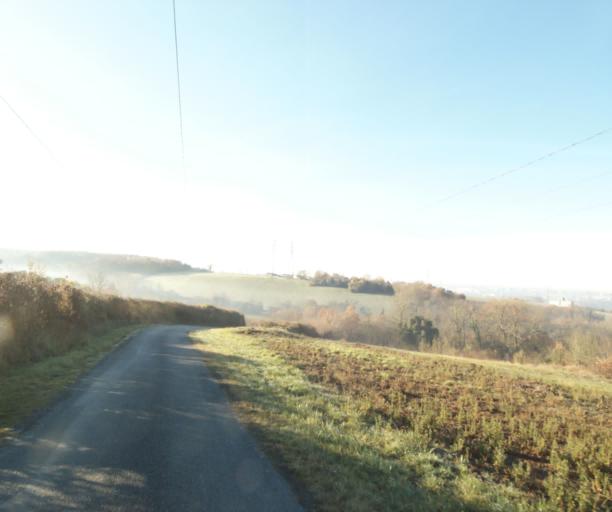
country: FR
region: Poitou-Charentes
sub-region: Departement de la Charente-Maritime
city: Fontcouverte
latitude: 45.7605
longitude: -0.6088
